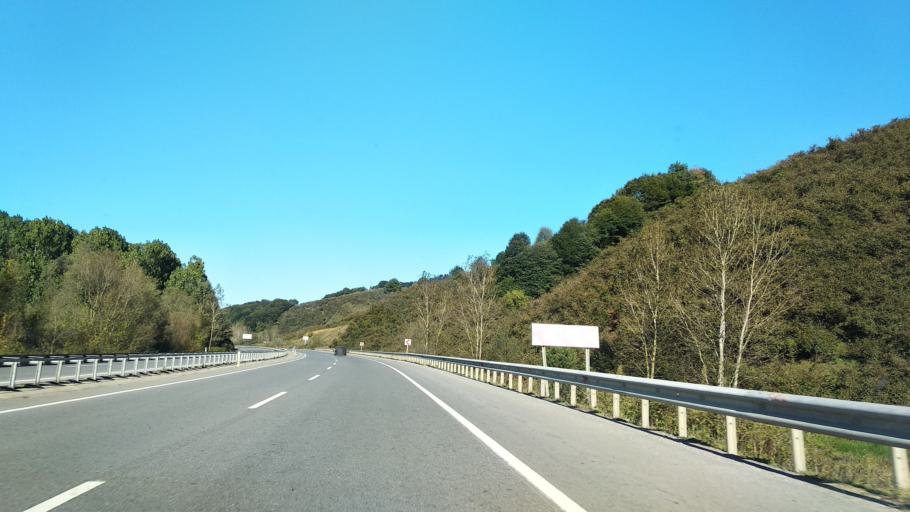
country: TR
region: Sakarya
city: Karasu
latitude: 41.0648
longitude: 30.6418
